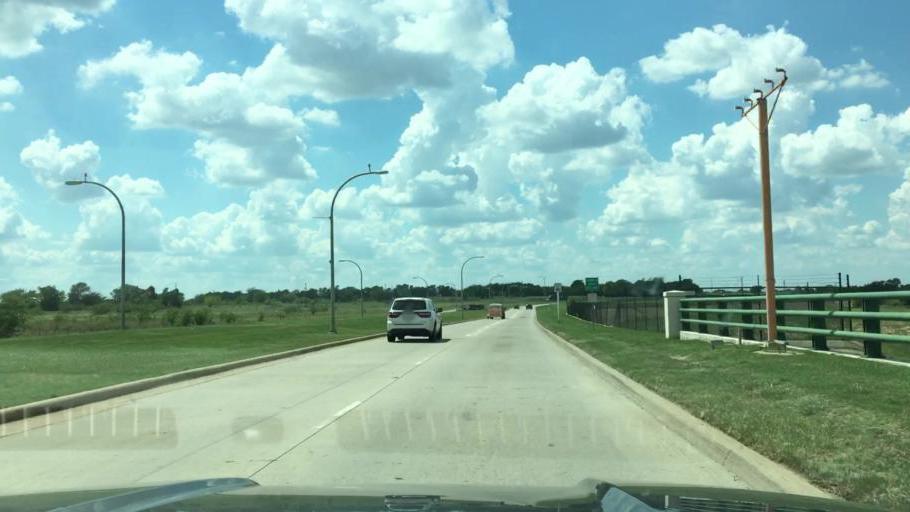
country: US
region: Texas
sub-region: Tarrant County
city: Haslet
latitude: 32.9725
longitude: -97.3149
